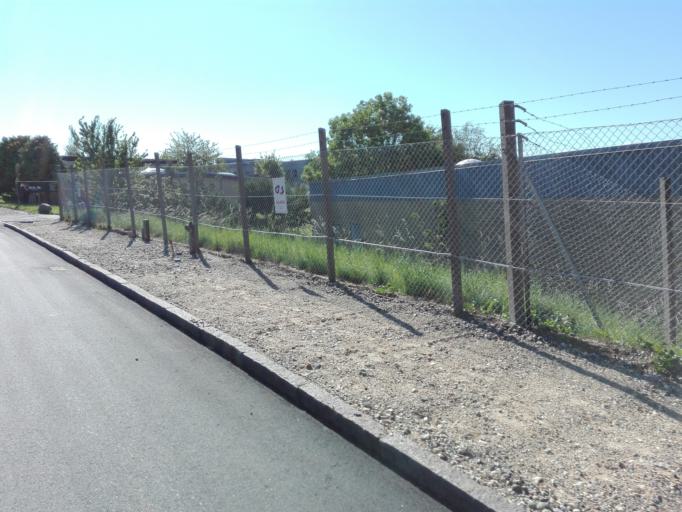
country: DK
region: Central Jutland
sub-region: Arhus Kommune
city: Tranbjerg
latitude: 56.1053
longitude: 10.1501
